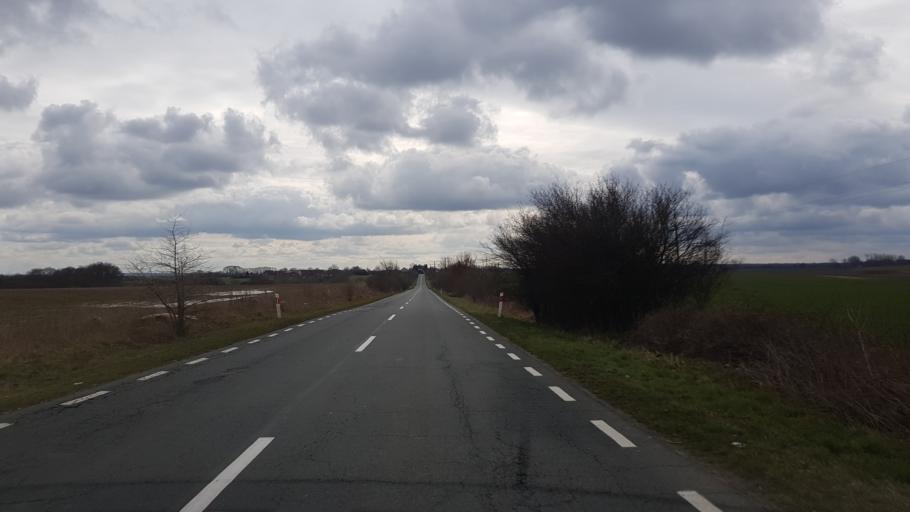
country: PL
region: West Pomeranian Voivodeship
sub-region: Powiat gryfinski
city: Banie
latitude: 53.1425
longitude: 14.6086
